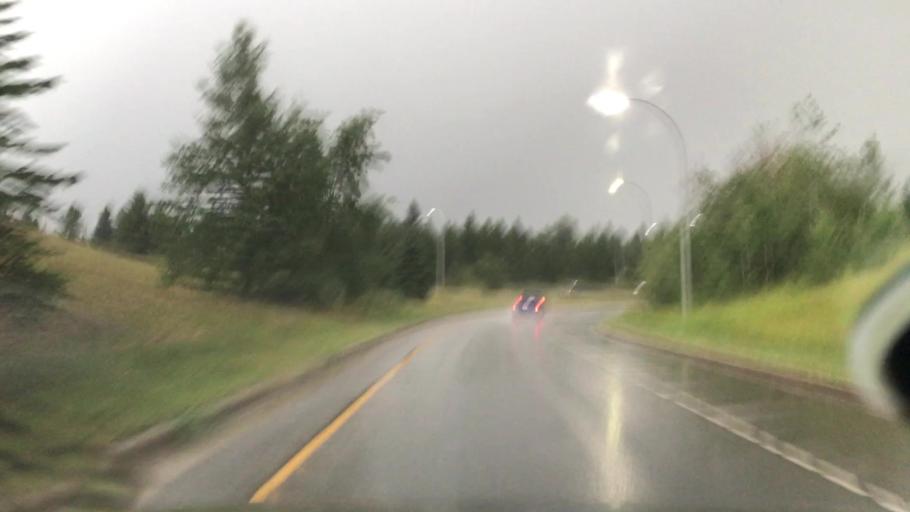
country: CA
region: Alberta
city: Edmonton
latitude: 53.4816
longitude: -113.5701
